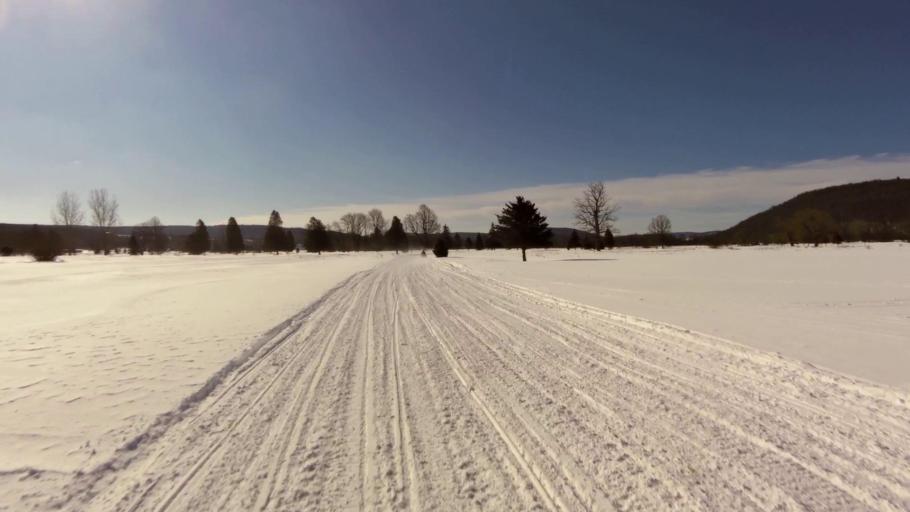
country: US
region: New York
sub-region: Cattaraugus County
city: Franklinville
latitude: 42.3603
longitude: -78.4570
